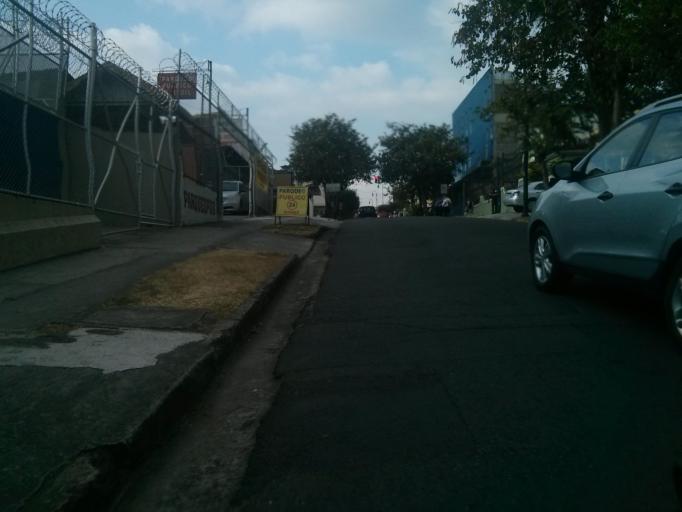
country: CR
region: San Jose
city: San Jose
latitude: 9.9323
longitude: -84.0700
